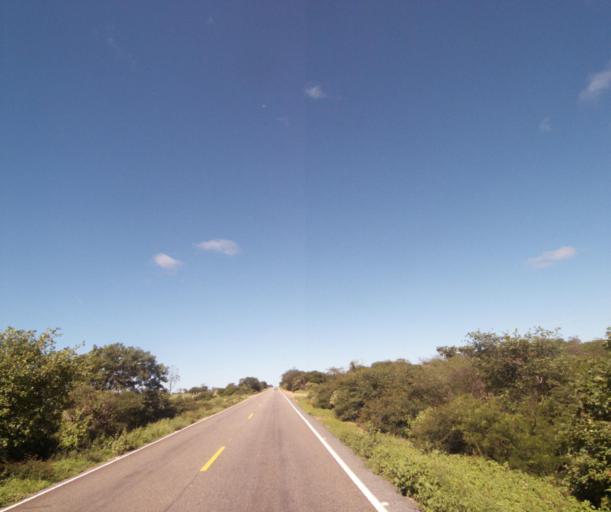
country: BR
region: Bahia
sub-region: Palmas De Monte Alto
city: Palmas de Monte Alto
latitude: -14.2450
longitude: -43.1063
